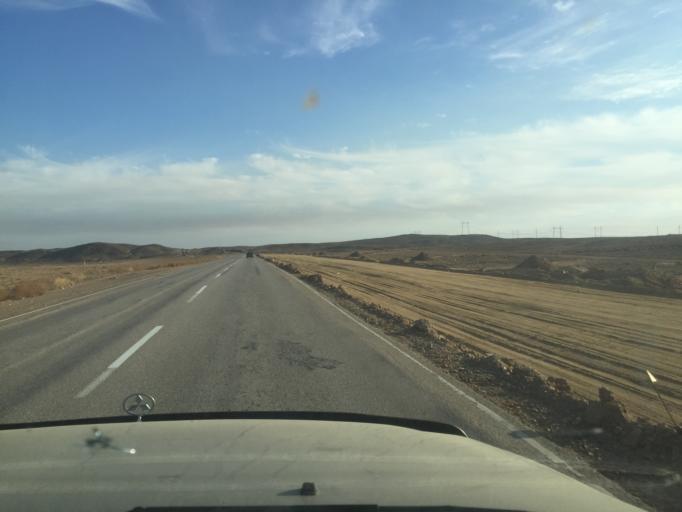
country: KZ
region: Zhambyl
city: Mynaral
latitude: 45.5167
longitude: 73.4923
